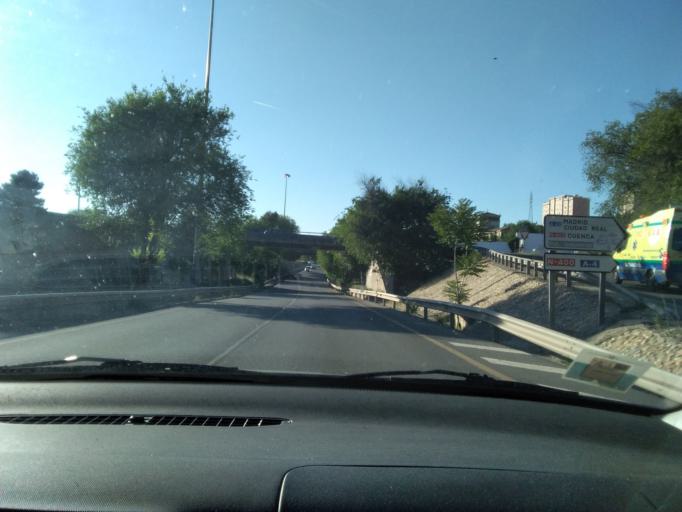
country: ES
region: Castille-La Mancha
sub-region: Province of Toledo
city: Toledo
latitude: 39.8741
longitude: -4.0416
